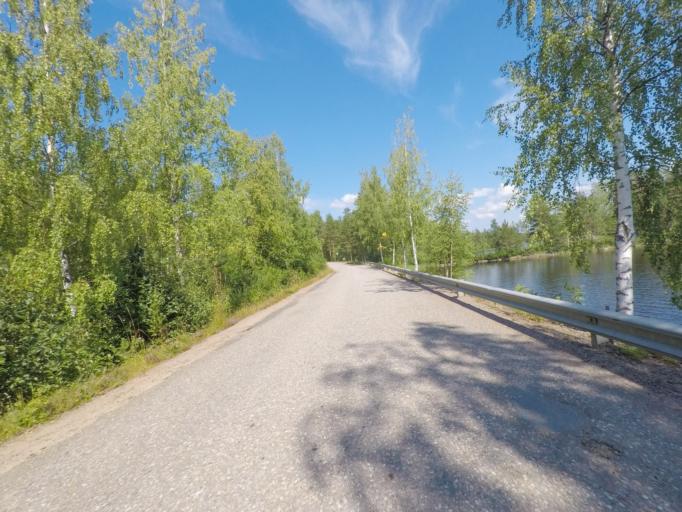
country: FI
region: Southern Savonia
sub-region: Mikkeli
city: Puumala
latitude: 61.4096
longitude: 28.0914
